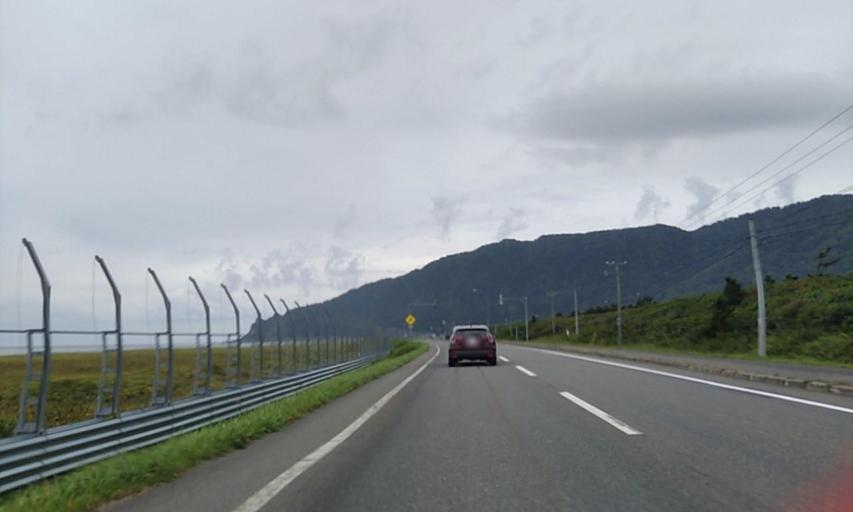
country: JP
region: Hokkaido
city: Makubetsu
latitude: 45.0748
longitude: 142.4642
